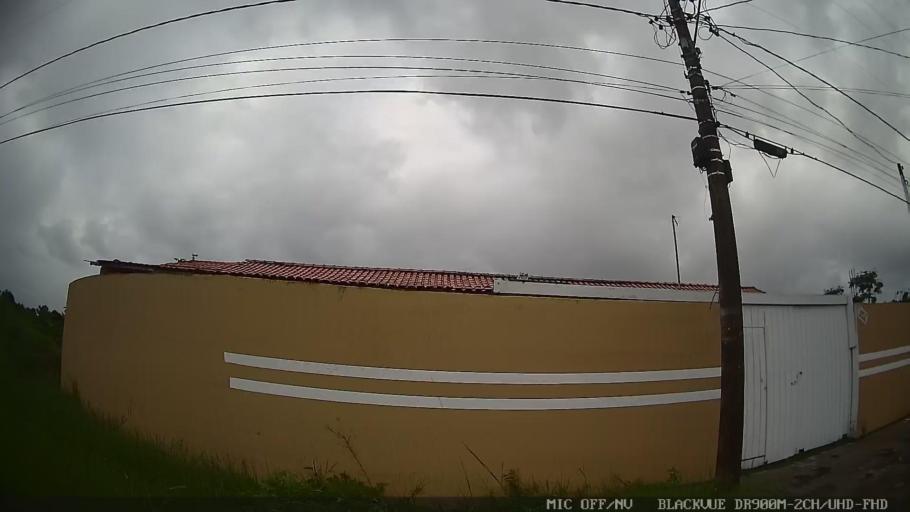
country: BR
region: Sao Paulo
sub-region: Itanhaem
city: Itanhaem
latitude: -24.2155
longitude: -46.8596
